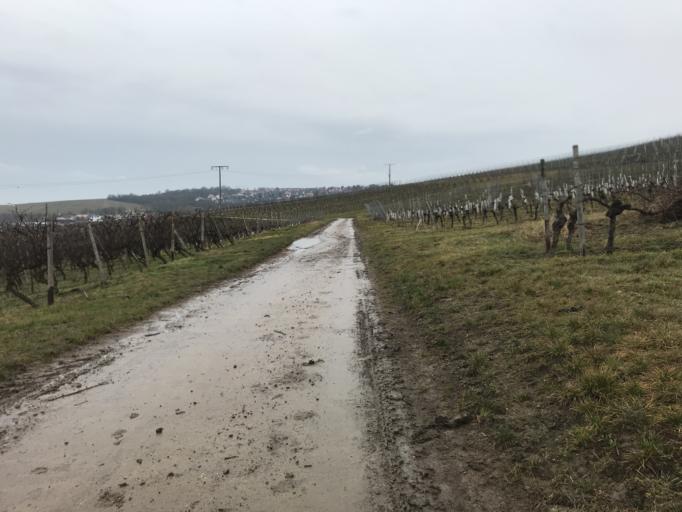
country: DE
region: Rheinland-Pfalz
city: Essenheim
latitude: 49.9323
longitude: 8.1685
